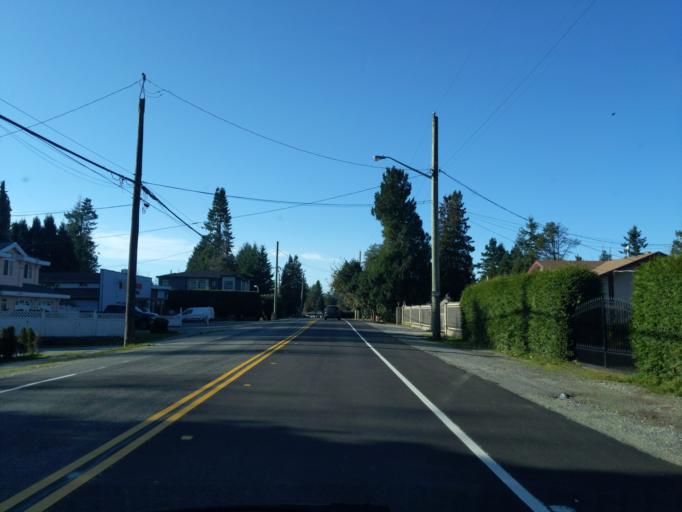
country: CA
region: British Columbia
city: New Westminster
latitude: 49.1884
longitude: -122.8591
